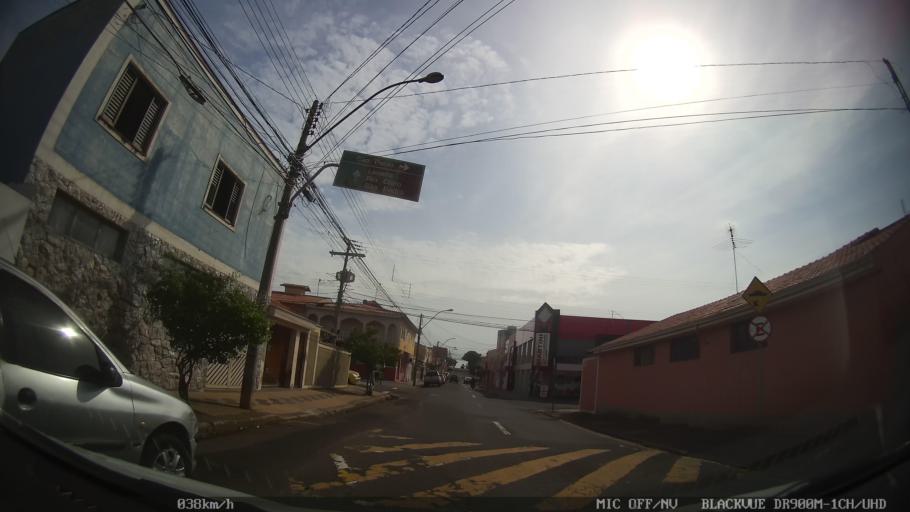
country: BR
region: Sao Paulo
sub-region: Piracicaba
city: Piracicaba
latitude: -22.7460
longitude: -47.6496
